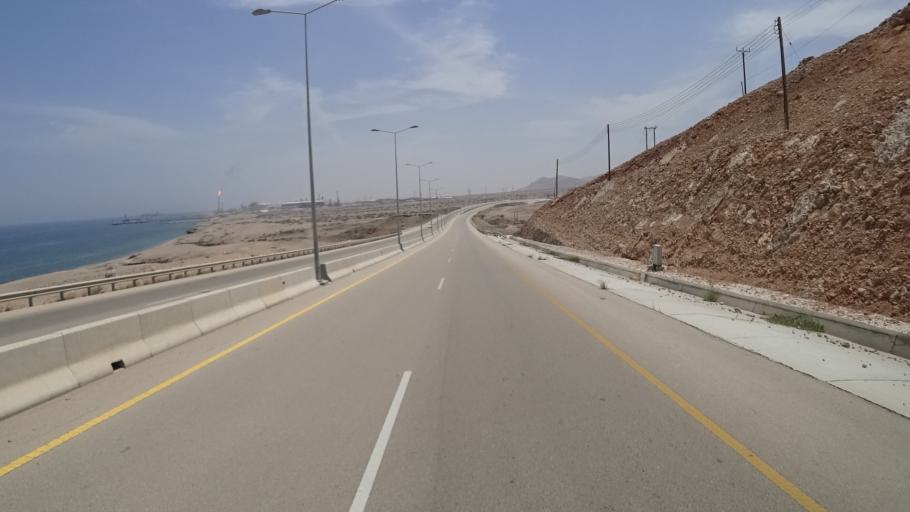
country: OM
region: Ash Sharqiyah
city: Sur
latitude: 22.6766
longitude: 59.3852
